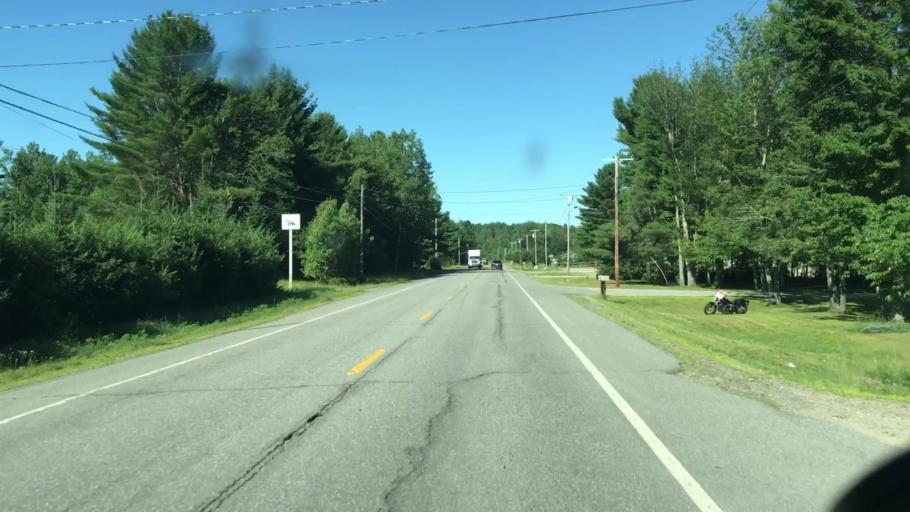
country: US
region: Maine
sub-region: Penobscot County
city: Lincoln
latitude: 45.3430
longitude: -68.5628
